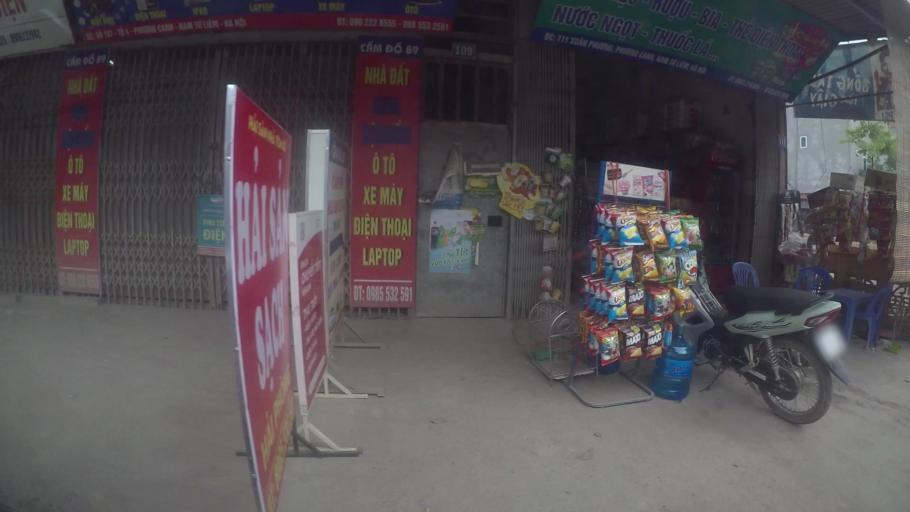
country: VN
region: Ha Noi
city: Cau Dien
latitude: 21.0395
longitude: 105.7380
